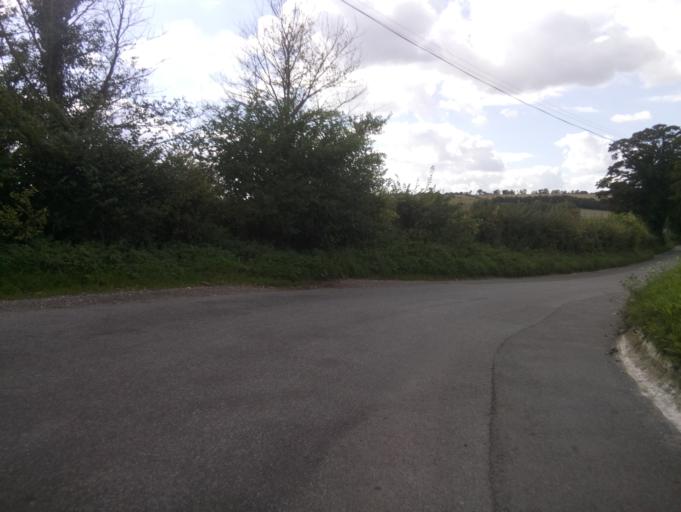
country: GB
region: England
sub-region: Wiltshire
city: Salisbury
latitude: 51.0947
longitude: -1.8102
